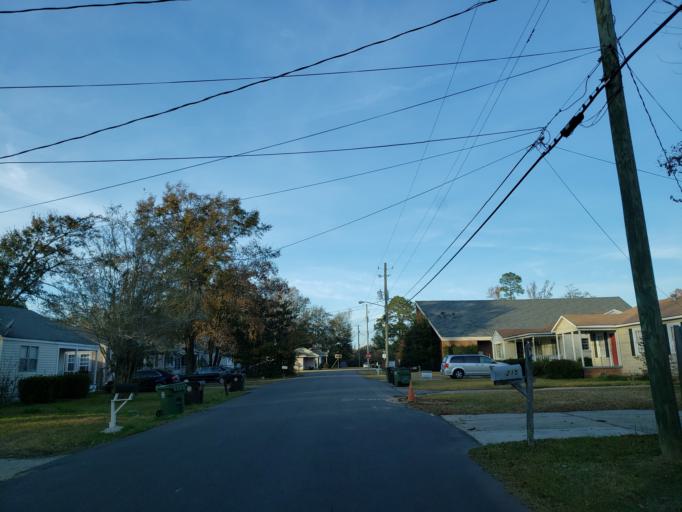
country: US
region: Mississippi
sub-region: Forrest County
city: Hattiesburg
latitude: 31.3276
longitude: -89.3192
